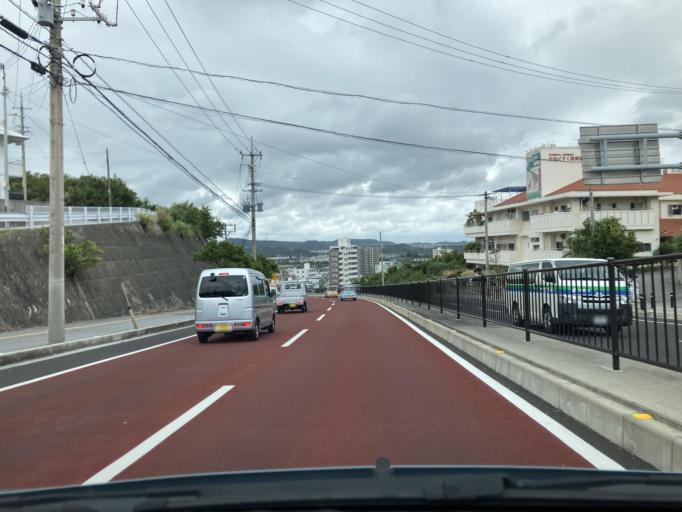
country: JP
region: Okinawa
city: Naha-shi
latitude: 26.2026
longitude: 127.7275
